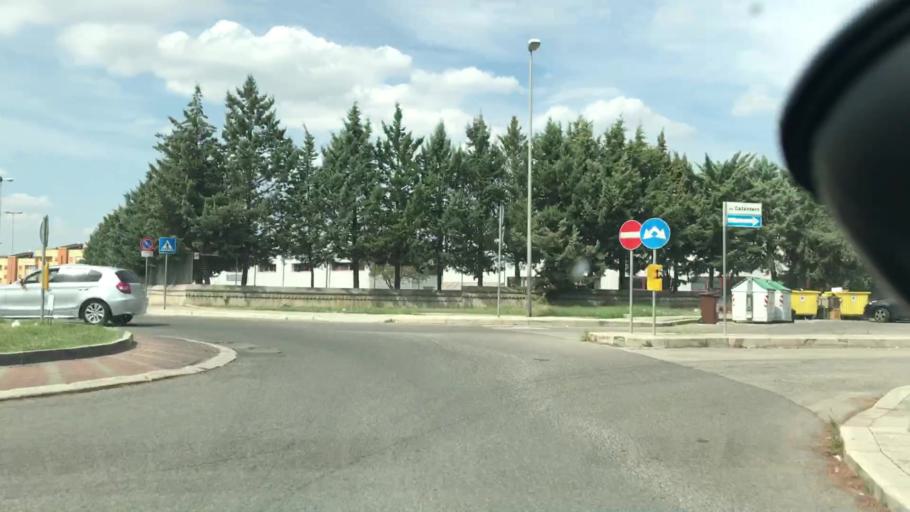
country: IT
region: Basilicate
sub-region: Provincia di Matera
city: Matera
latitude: 40.6790
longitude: 16.5806
